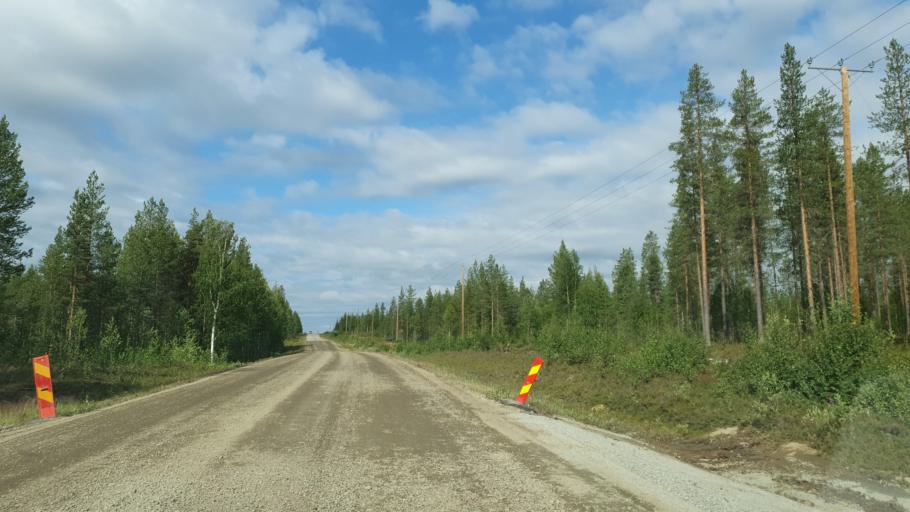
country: FI
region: Lapland
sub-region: Pohjois-Lappi
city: Sodankylae
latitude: 67.5359
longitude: 25.9690
